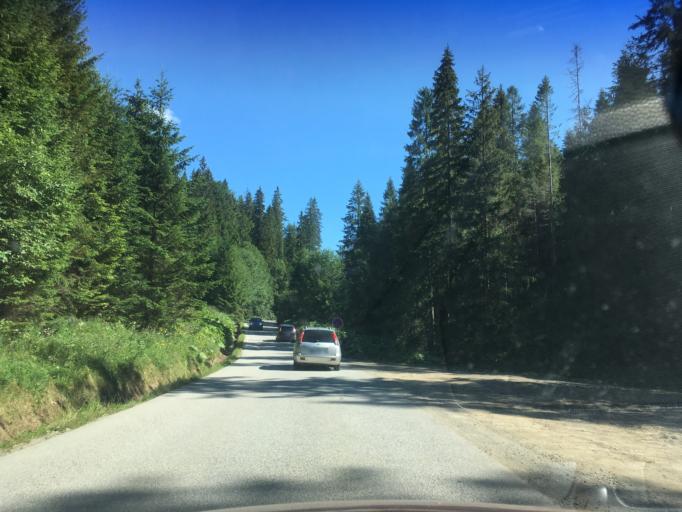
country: SK
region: Presovsky
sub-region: Okres Poprad
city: Zdiar
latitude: 49.2673
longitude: 20.3054
